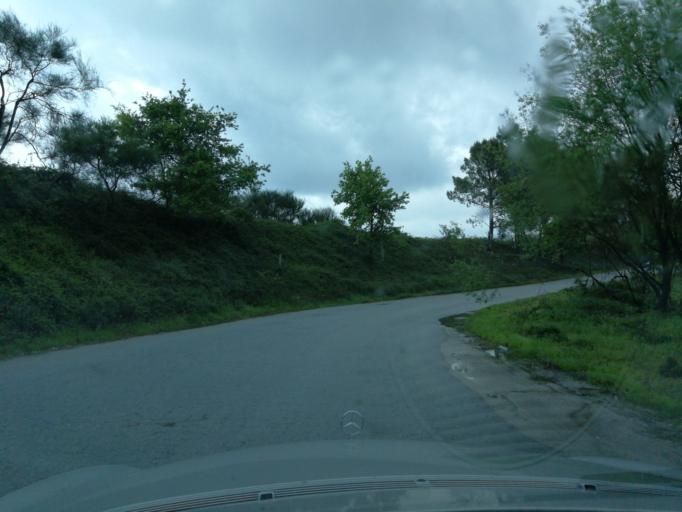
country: PT
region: Braga
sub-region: Vila Nova de Famalicao
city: Joane
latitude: 41.4625
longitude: -8.4323
